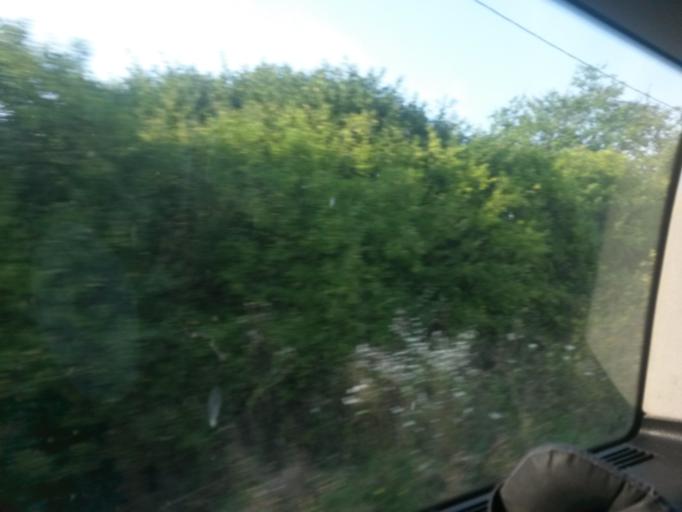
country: RO
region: Alba
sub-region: Municipiul Aiud
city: Aiudul de Sus
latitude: 46.3215
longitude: 23.6741
